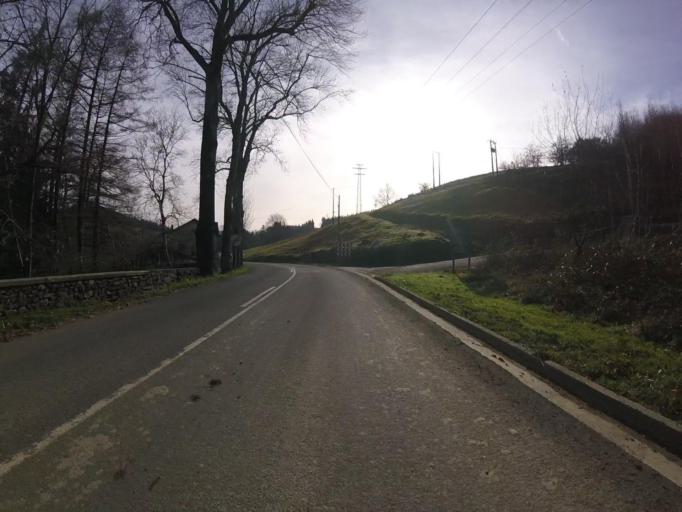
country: ES
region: Basque Country
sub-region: Provincia de Guipuzcoa
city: Berastegui
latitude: 43.1064
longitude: -1.9626
